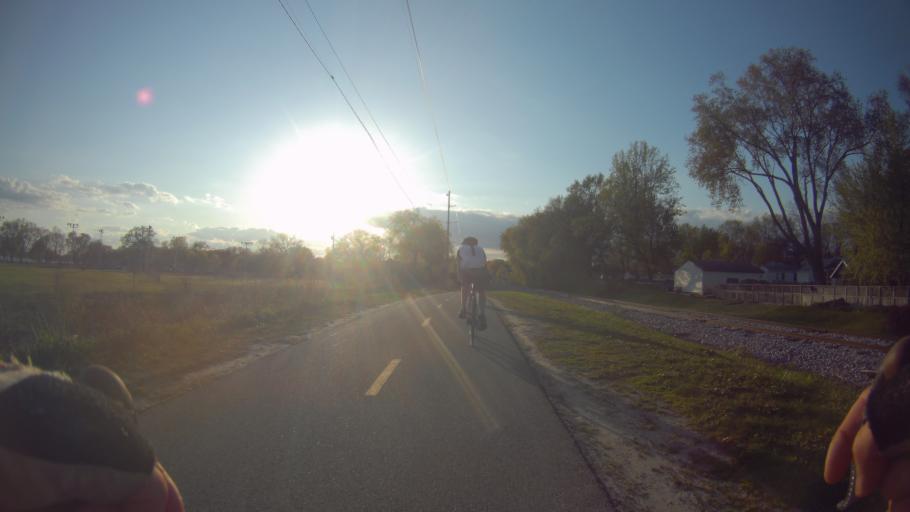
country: US
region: Wisconsin
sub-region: Dane County
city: Monona
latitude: 43.0921
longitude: -89.3299
